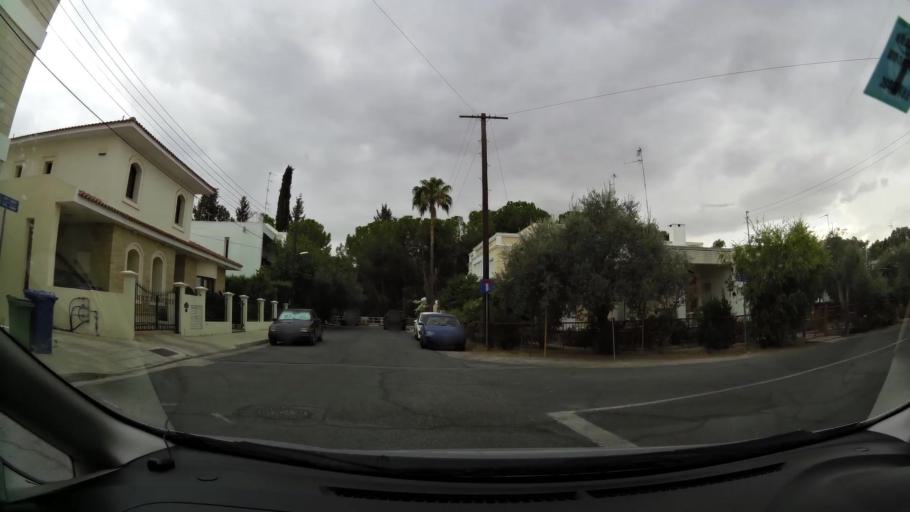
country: CY
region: Lefkosia
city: Nicosia
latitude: 35.1545
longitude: 33.3565
